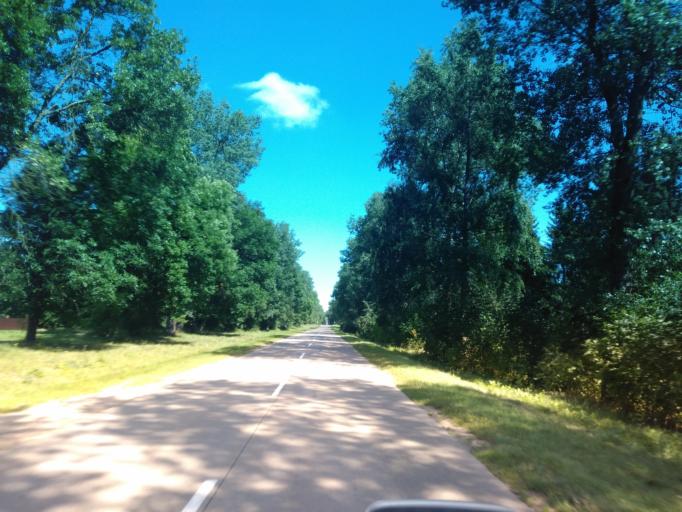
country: BY
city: Fanipol
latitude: 53.6614
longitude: 27.3270
